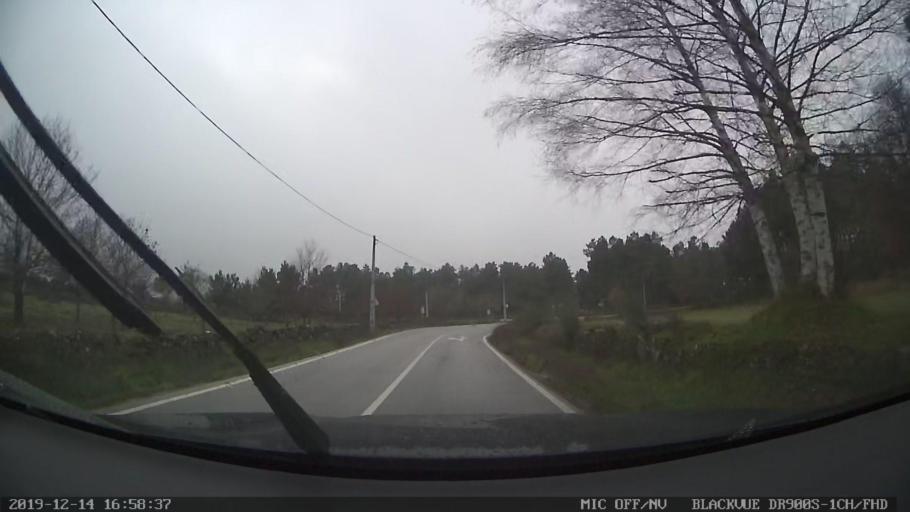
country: PT
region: Vila Real
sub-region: Murca
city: Murca
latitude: 41.4358
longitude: -7.5540
